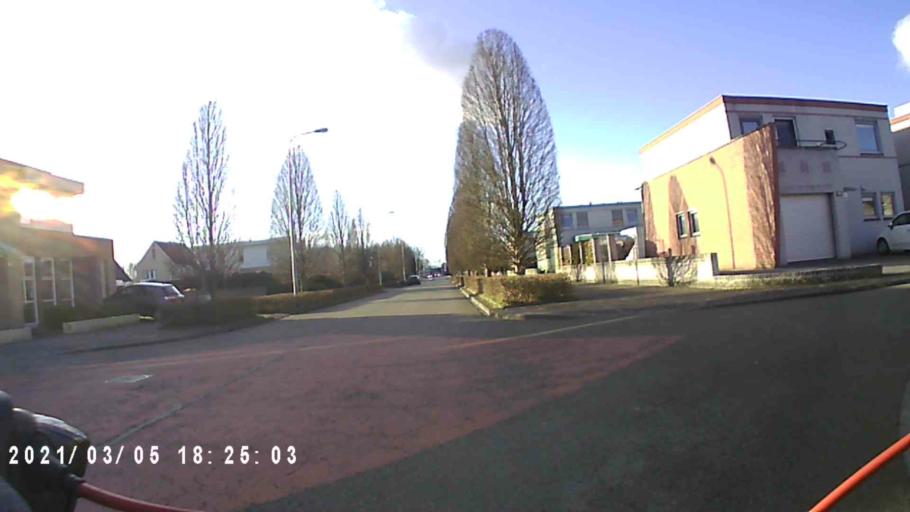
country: NL
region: Groningen
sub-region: Gemeente Groningen
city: Korrewegwijk
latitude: 53.2416
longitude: 6.5759
